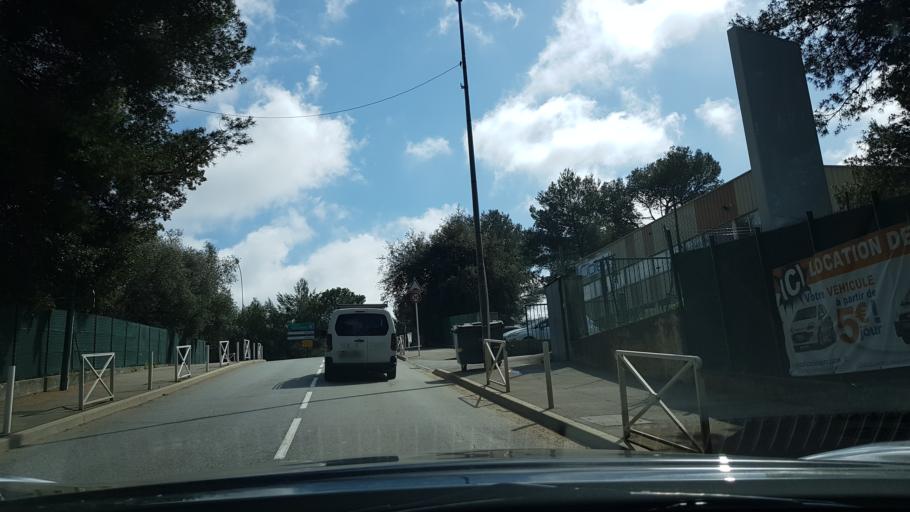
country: FR
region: Provence-Alpes-Cote d'Azur
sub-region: Departement des Alpes-Maritimes
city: Biot
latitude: 43.6038
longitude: 7.0772
